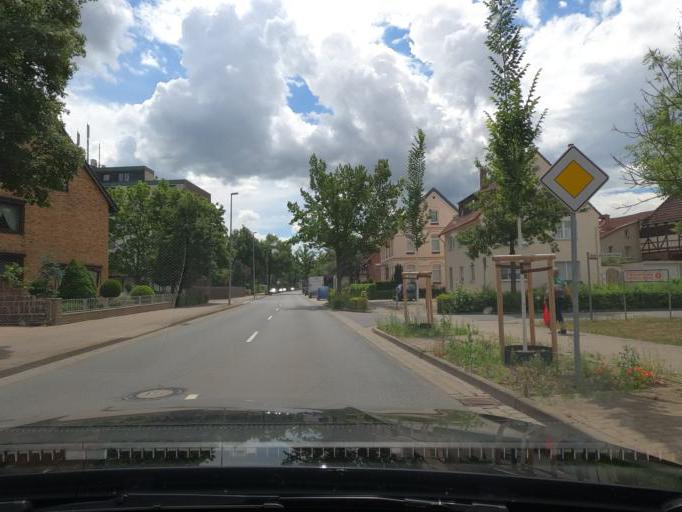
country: DE
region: Lower Saxony
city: Sehnde
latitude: 52.3132
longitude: 9.9638
